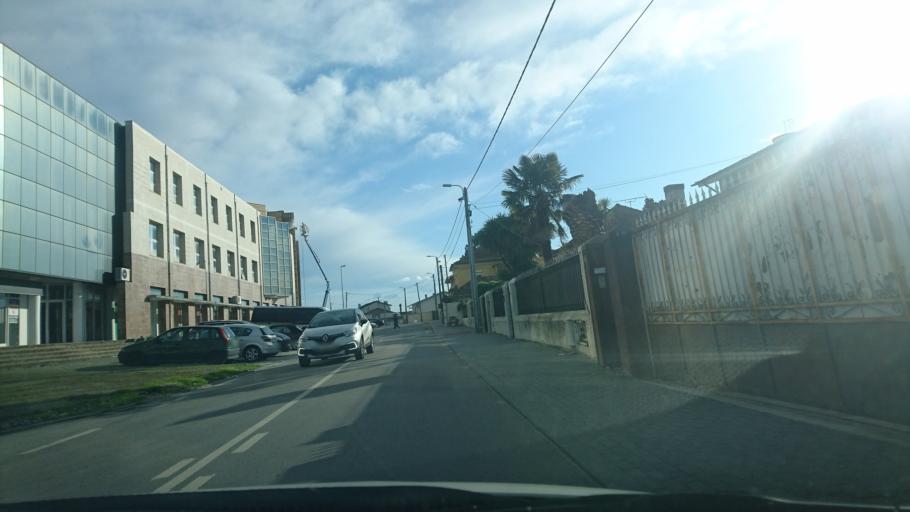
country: PT
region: Aveiro
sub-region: Santa Maria da Feira
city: Pacos de Brandao
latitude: 40.9734
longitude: -8.5792
